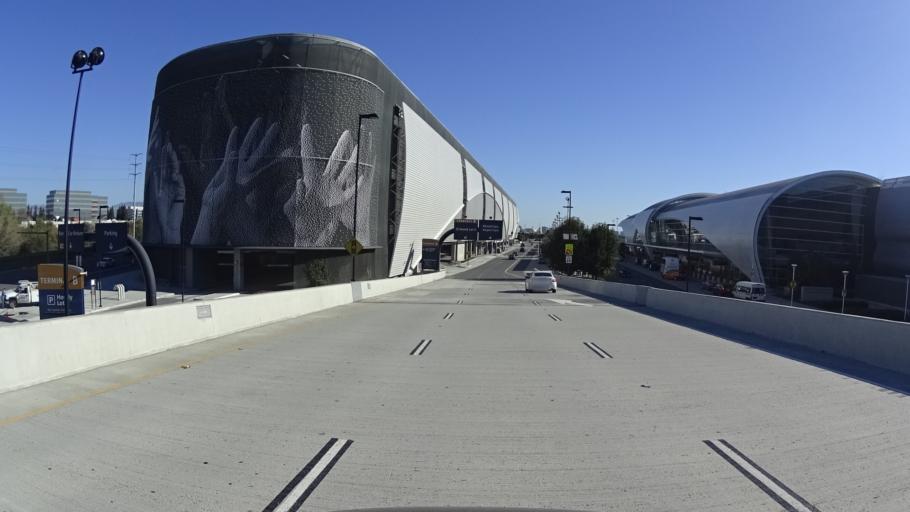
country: US
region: California
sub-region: Santa Clara County
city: Santa Clara
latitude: 37.3662
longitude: -121.9249
